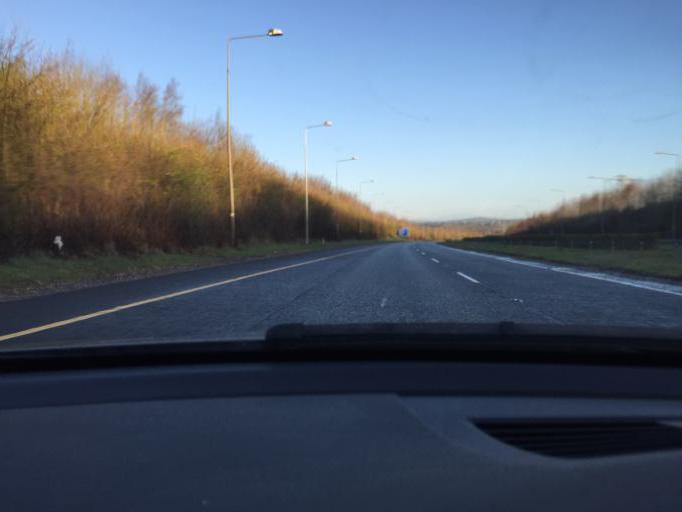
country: IE
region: Leinster
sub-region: Lu
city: Tullyallen
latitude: 53.7062
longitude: -6.3905
